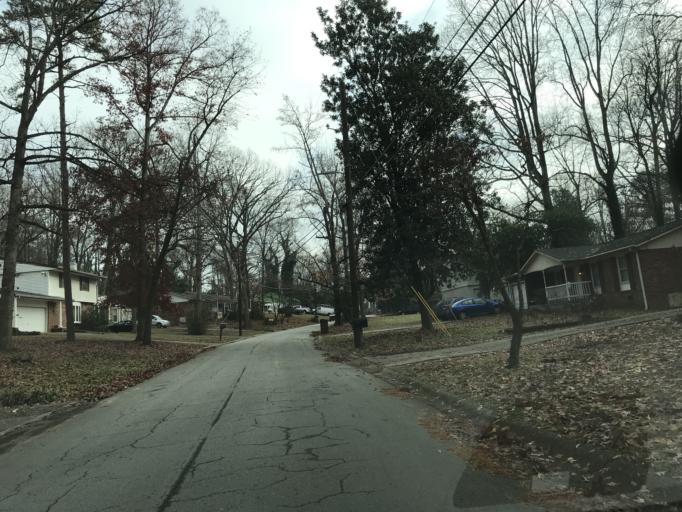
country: US
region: Georgia
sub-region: Clayton County
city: Riverdale
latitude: 33.5596
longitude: -84.3747
